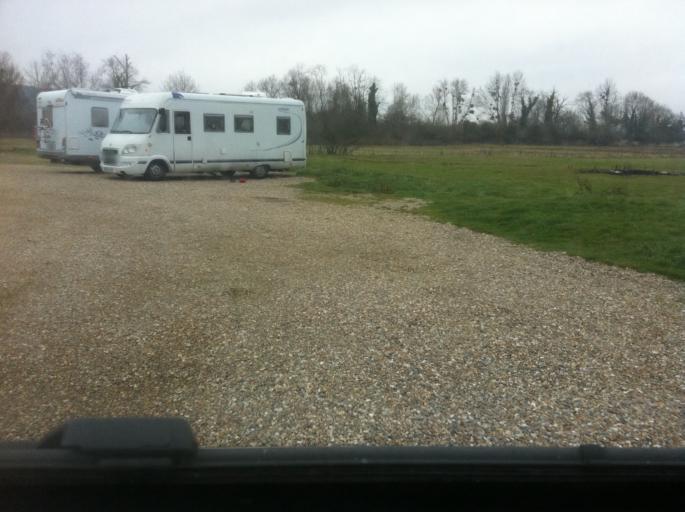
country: FR
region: Haute-Normandie
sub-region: Departement de la Seine-Maritime
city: Jumieges
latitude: 49.4309
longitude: 0.8149
